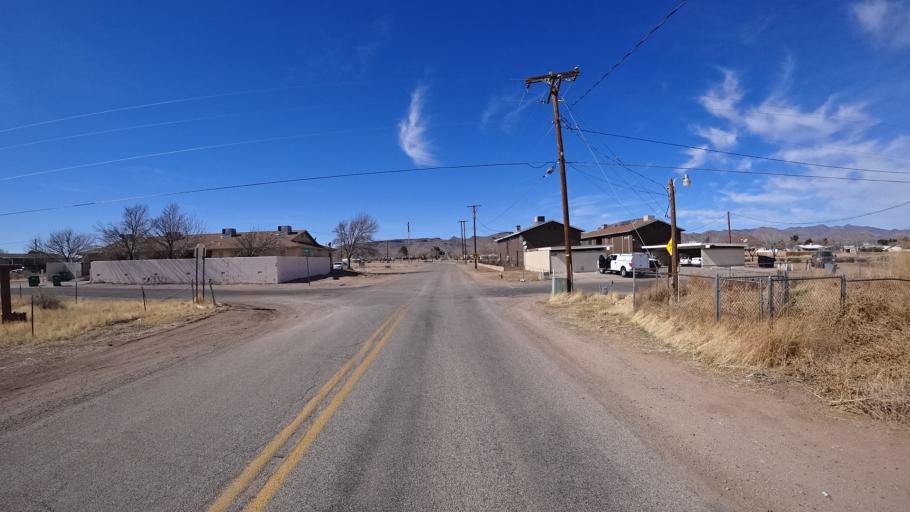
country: US
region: Arizona
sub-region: Mohave County
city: New Kingman-Butler
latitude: 35.2468
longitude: -114.0130
